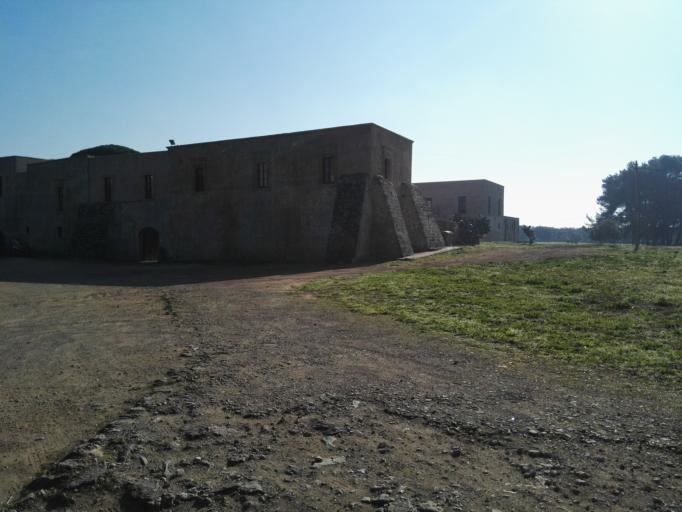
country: IT
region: Apulia
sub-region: Provincia di Lecce
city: Trepuzzi
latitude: 40.4589
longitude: 18.1148
